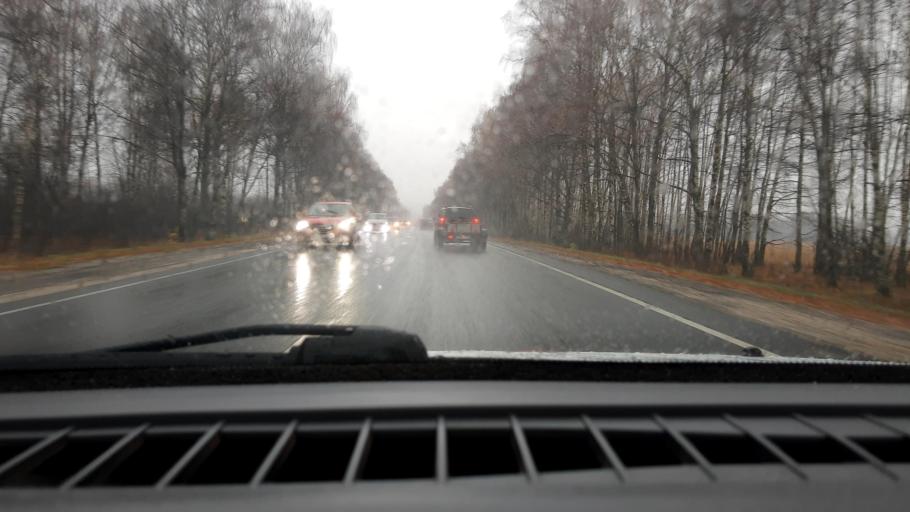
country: RU
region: Nizjnij Novgorod
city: Sitniki
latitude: 56.5372
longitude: 44.0209
